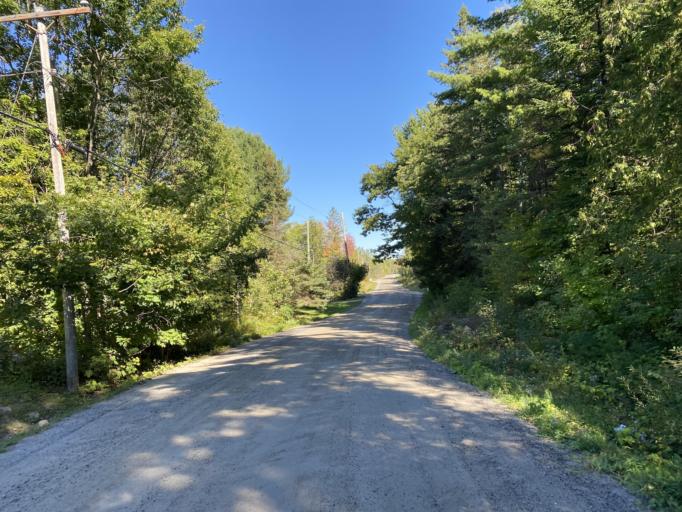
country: CA
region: Quebec
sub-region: Outaouais
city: Val-des-Monts
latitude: 45.5670
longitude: -75.5319
